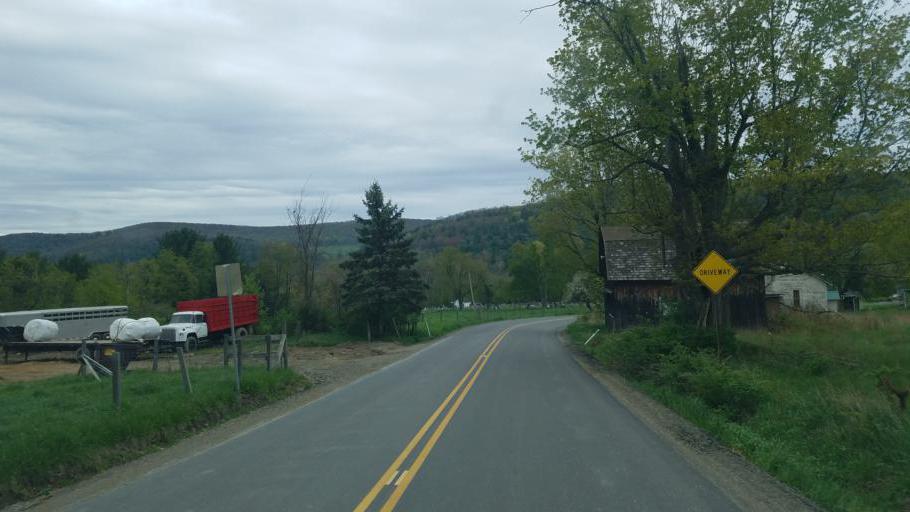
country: US
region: Pennsylvania
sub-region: Tioga County
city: Westfield
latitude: 41.9962
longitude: -77.4897
